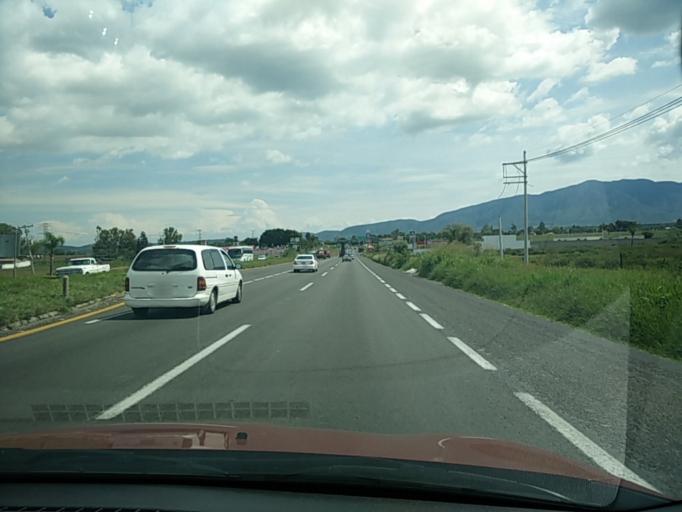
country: MX
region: Jalisco
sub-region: Ixtlahuacan de los Membrillos
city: Los Olivos
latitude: 20.4237
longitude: -103.2374
